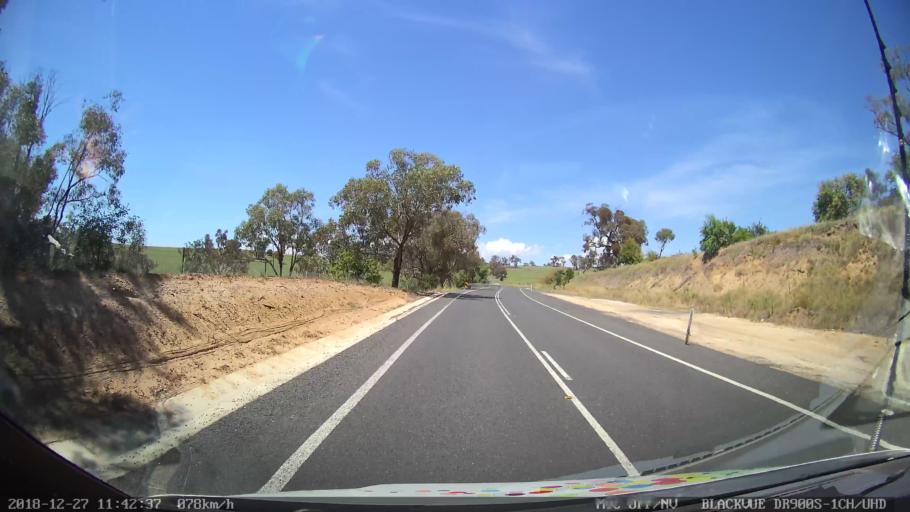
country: AU
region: New South Wales
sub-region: Bathurst Regional
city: Perthville
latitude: -33.5506
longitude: 149.4779
